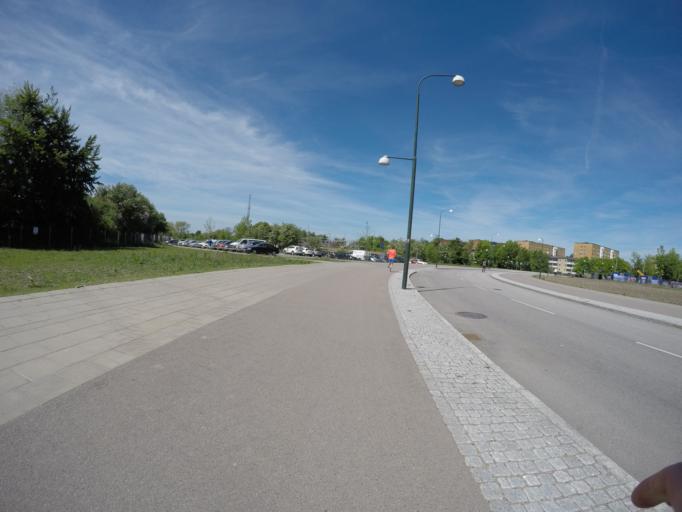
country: SE
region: Skane
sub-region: Malmo
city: Malmoe
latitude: 55.5706
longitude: 12.9748
